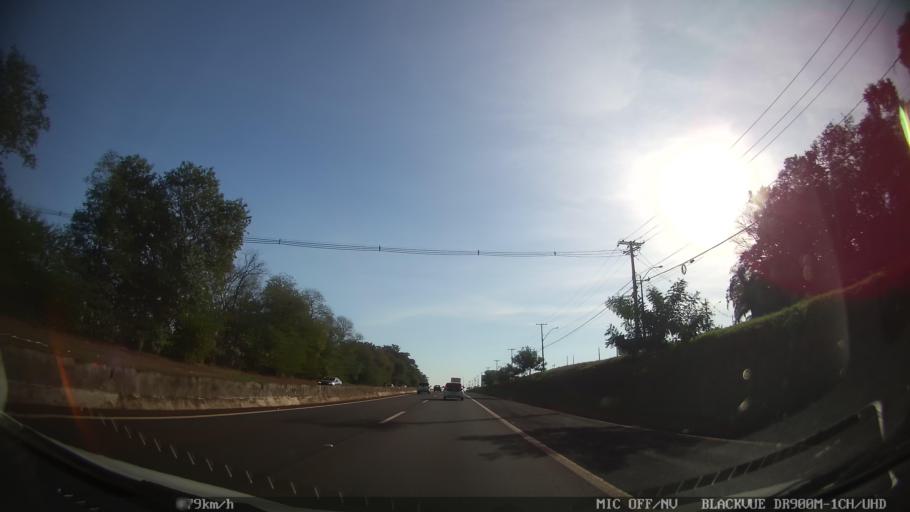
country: BR
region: Sao Paulo
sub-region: Ribeirao Preto
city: Ribeirao Preto
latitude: -21.2328
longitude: -47.8183
